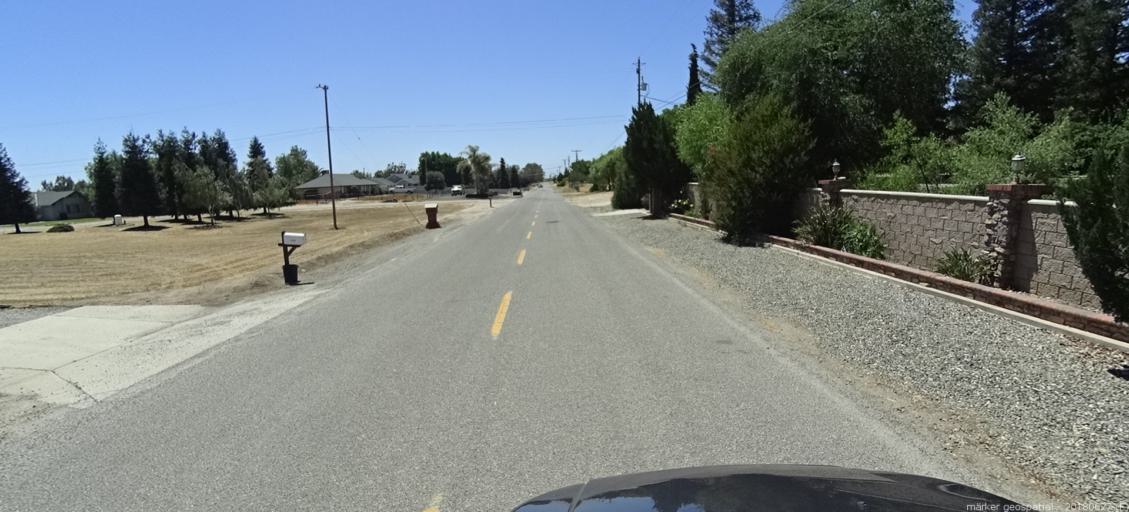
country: US
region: California
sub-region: Madera County
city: Bonadelle Ranchos-Madera Ranchos
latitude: 36.9642
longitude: -119.9061
